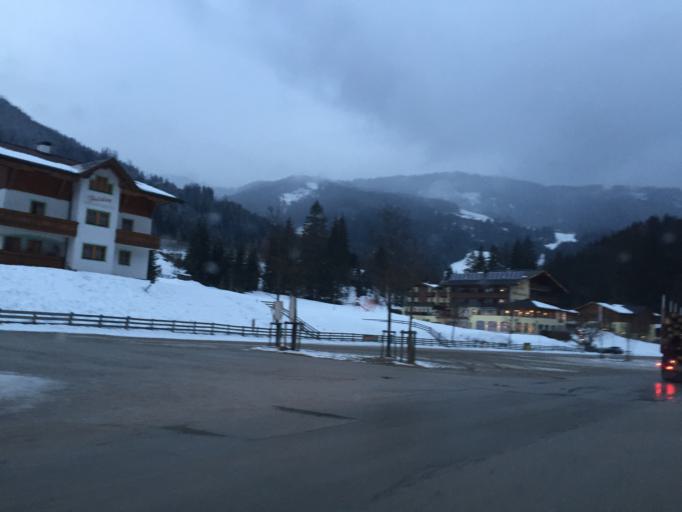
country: AT
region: Salzburg
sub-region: Politischer Bezirk Sankt Johann im Pongau
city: Flachau
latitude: 47.2939
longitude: 13.3987
